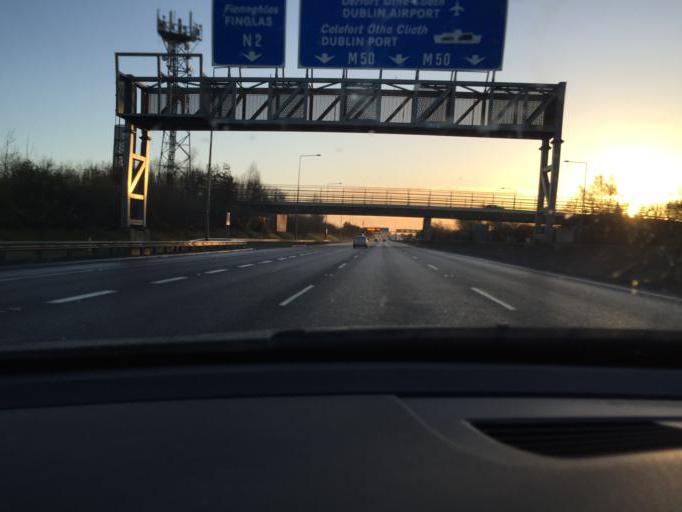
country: IE
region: Leinster
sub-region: Dublin City
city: Finglas
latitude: 53.3965
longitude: -6.3327
